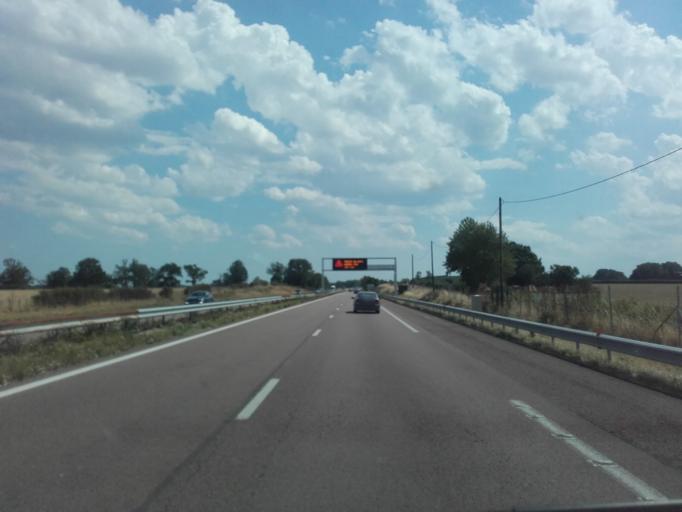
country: FR
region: Bourgogne
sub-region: Departement de l'Yonne
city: Avallon
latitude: 47.5360
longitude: 3.9779
